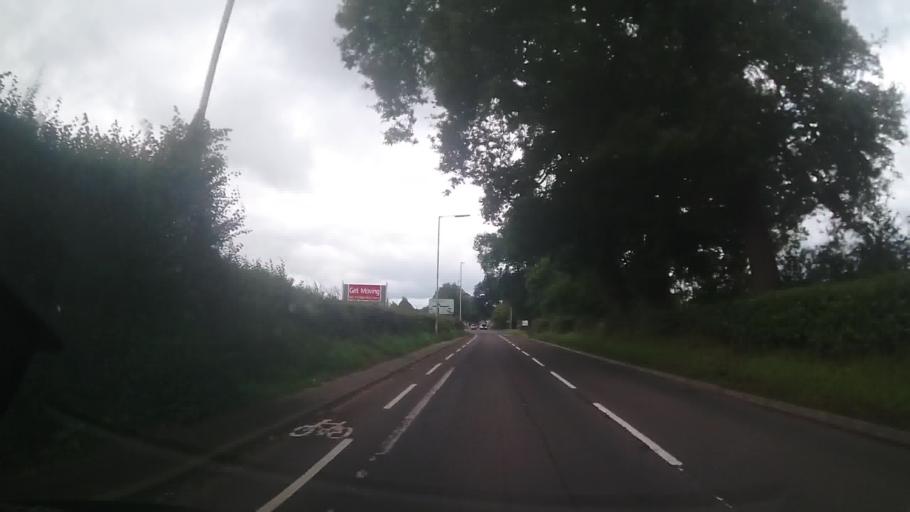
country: GB
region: England
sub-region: Shropshire
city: Whitchurch
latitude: 52.9596
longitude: -2.6762
